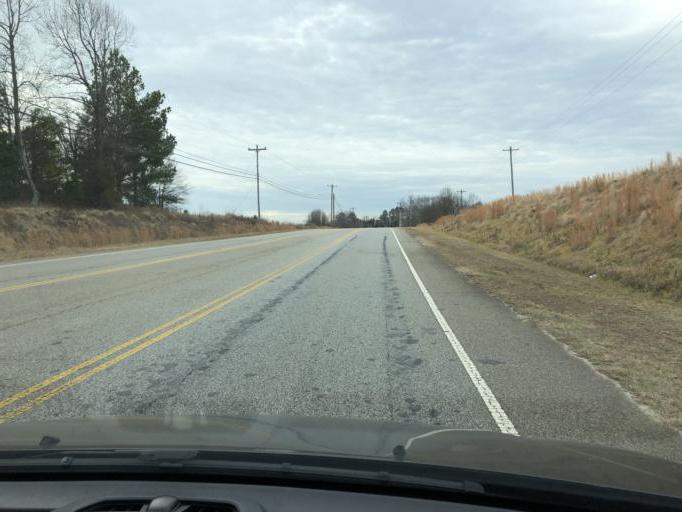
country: US
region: South Carolina
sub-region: Greenville County
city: Greer
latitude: 34.8826
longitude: -82.1953
